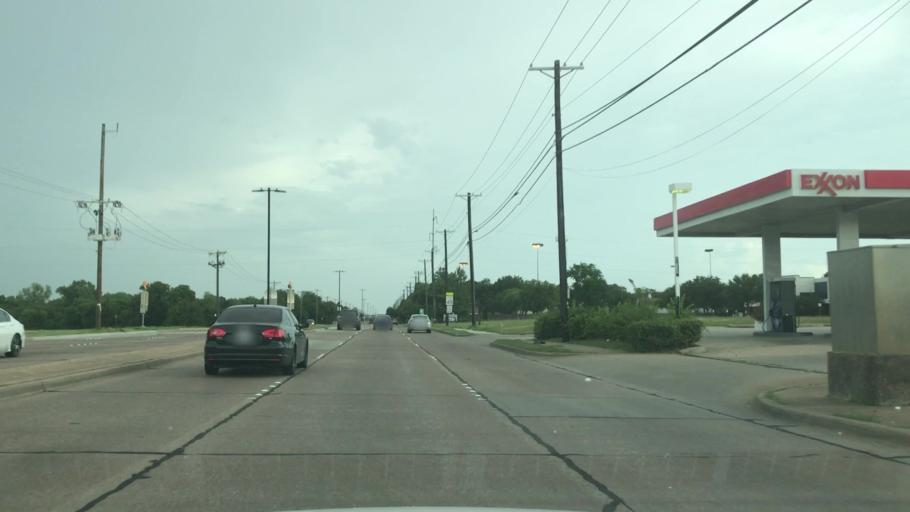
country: US
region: Texas
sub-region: Dallas County
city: Rowlett
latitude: 32.8573
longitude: -96.6022
